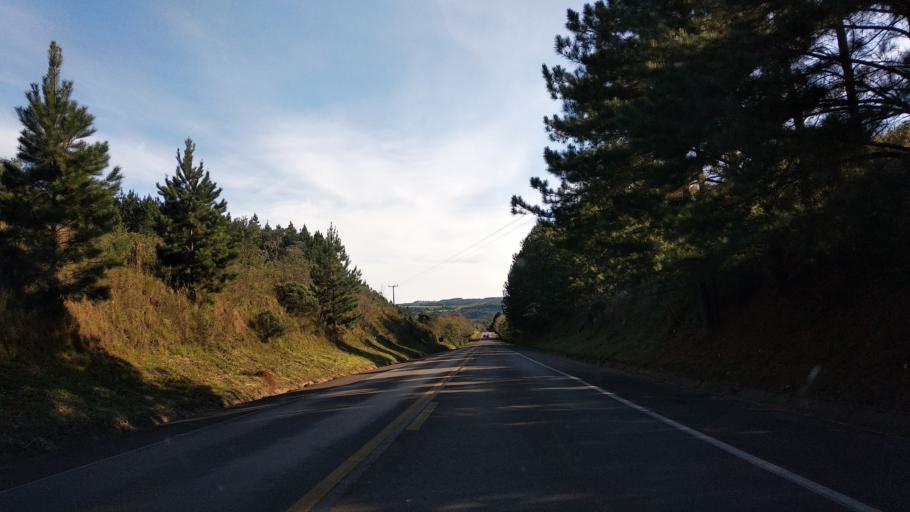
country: BR
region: Santa Catarina
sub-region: Celso Ramos
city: Celso Ramos
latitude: -27.5445
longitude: -51.4248
